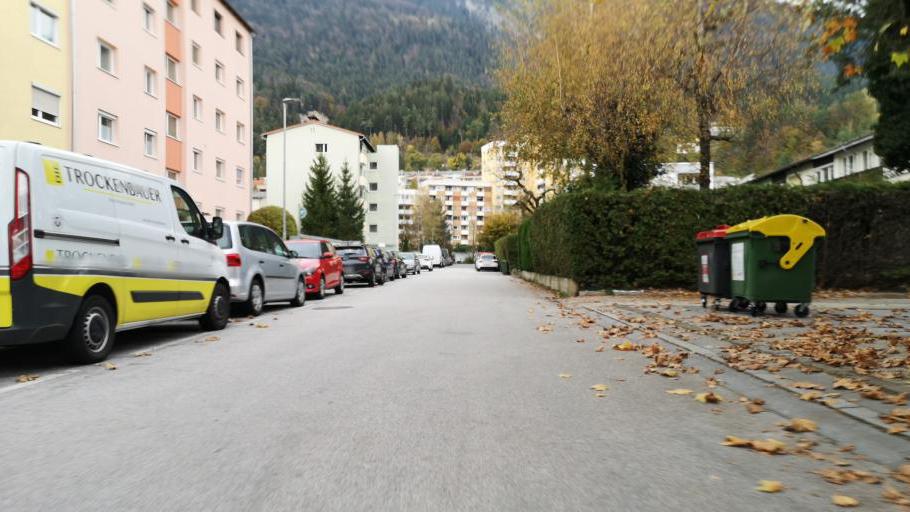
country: AT
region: Tyrol
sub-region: Politischer Bezirk Innsbruck Land
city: Vols
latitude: 47.2655
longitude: 11.3480
